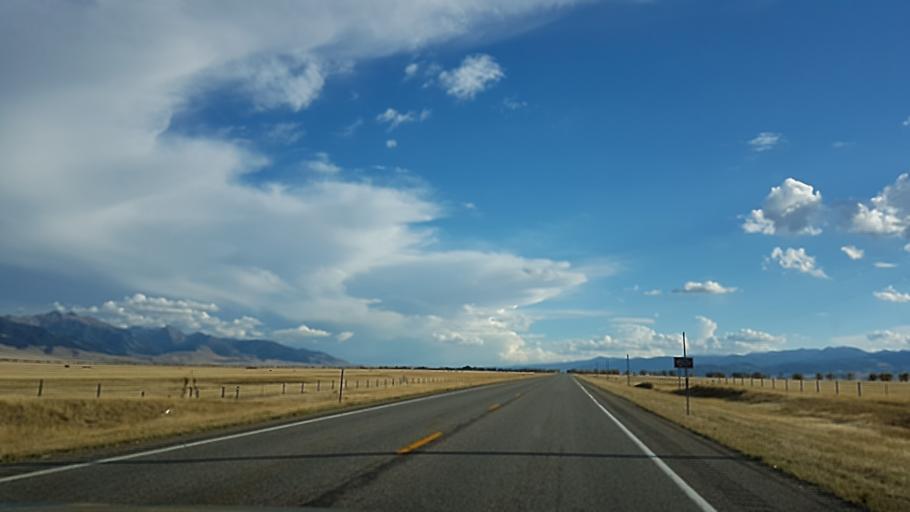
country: US
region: Montana
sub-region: Madison County
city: Virginia City
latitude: 45.2276
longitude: -111.6789
